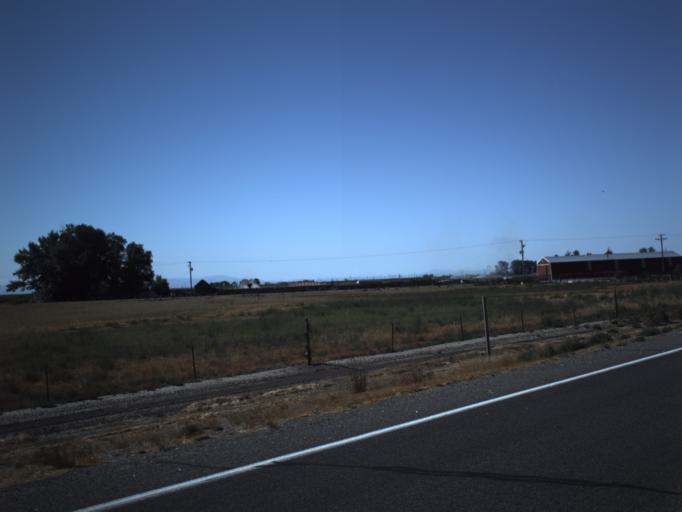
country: US
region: Utah
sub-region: Millard County
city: Delta
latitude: 39.3325
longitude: -112.6109
